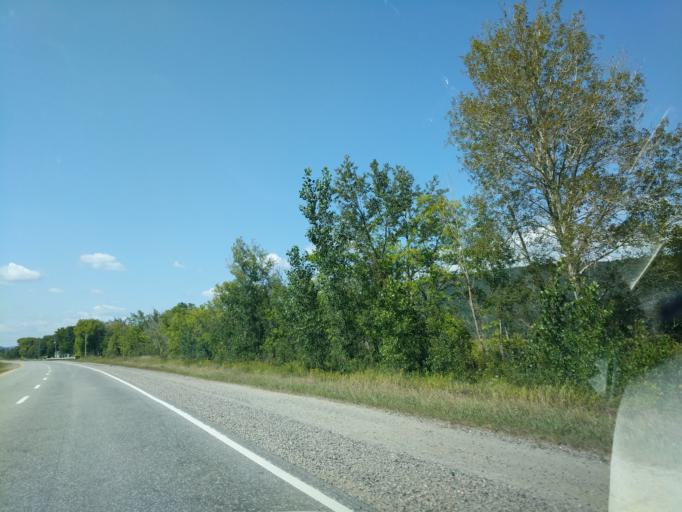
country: CA
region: Quebec
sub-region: Outaouais
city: Wakefield
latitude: 45.5239
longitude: -75.9928
